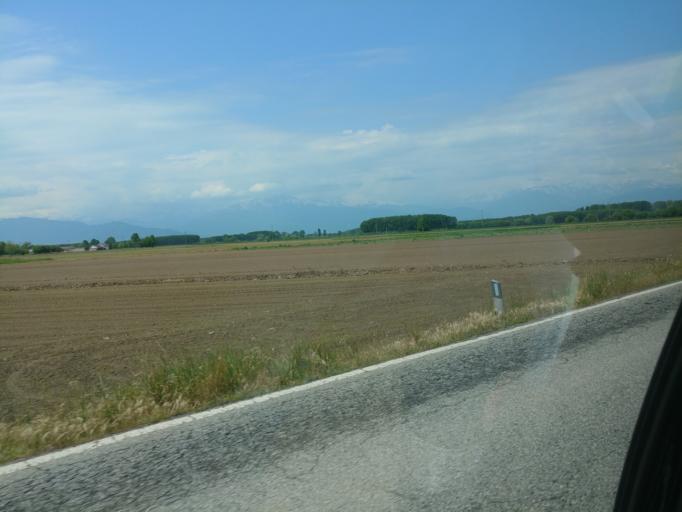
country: IT
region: Piedmont
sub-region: Provincia di Cuneo
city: Moretta
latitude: 44.7718
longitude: 7.5240
